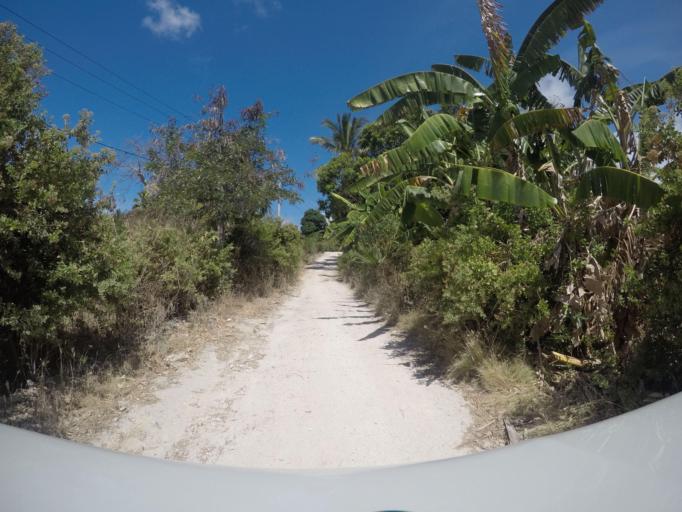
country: TL
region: Baucau
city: Baucau
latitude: -8.4535
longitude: 126.4413
